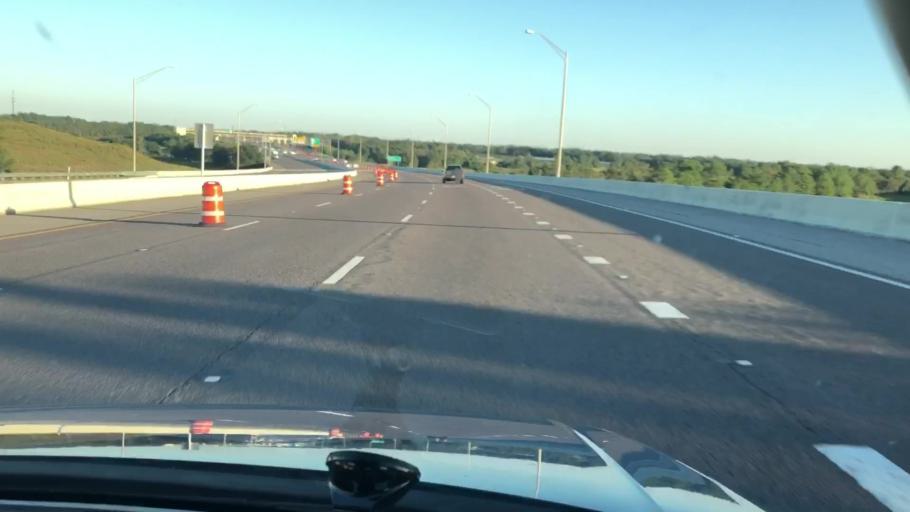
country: US
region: Florida
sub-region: Orange County
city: South Apopka
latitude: 28.6475
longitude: -81.5156
